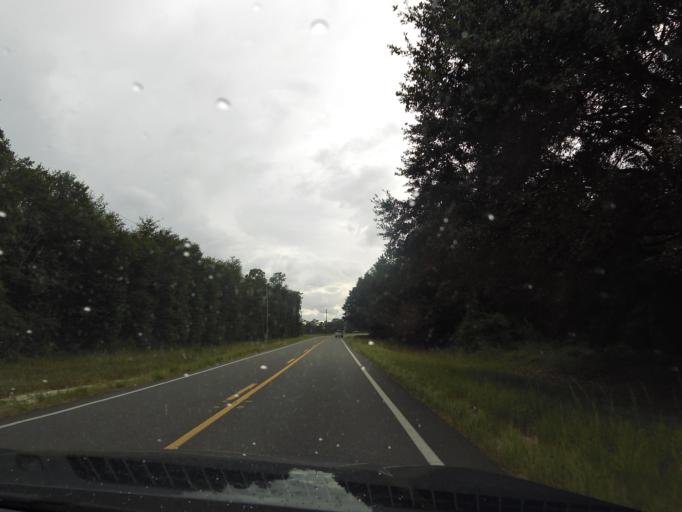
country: US
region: Florida
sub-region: Baker County
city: Macclenny
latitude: 30.3855
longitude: -82.1740
